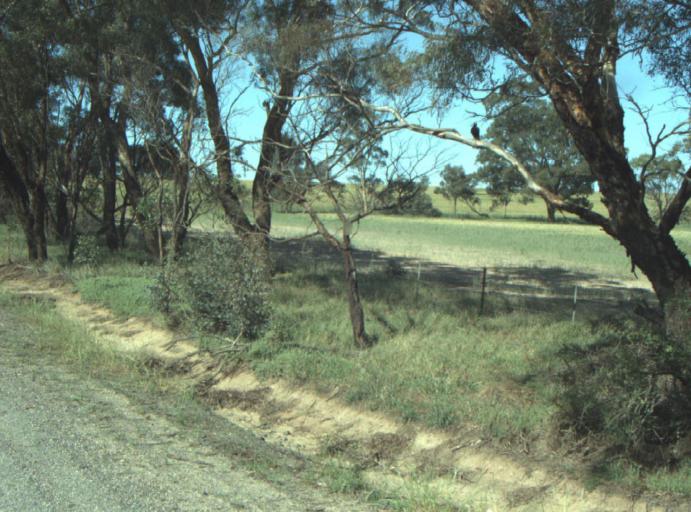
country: AU
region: Victoria
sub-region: Wyndham
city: Little River
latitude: -37.8972
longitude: 144.4010
